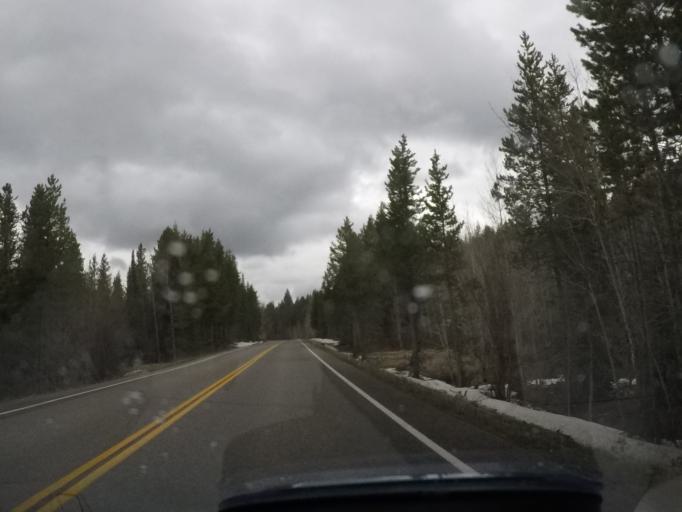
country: US
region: Wyoming
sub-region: Teton County
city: Moose Wilson Road
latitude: 43.9929
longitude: -110.6713
